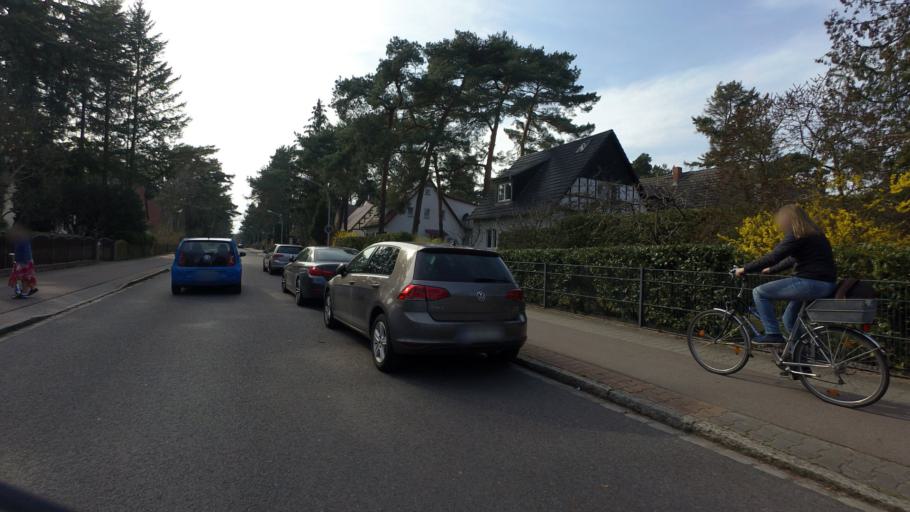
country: DE
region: Brandenburg
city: Kleinmachnow
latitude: 52.4134
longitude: 13.2192
